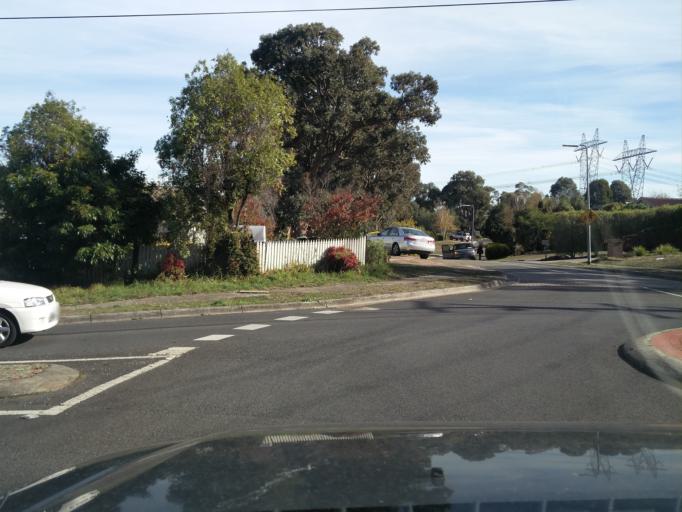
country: AU
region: Victoria
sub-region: Nillumbik
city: Research
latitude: -37.7088
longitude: 145.1754
